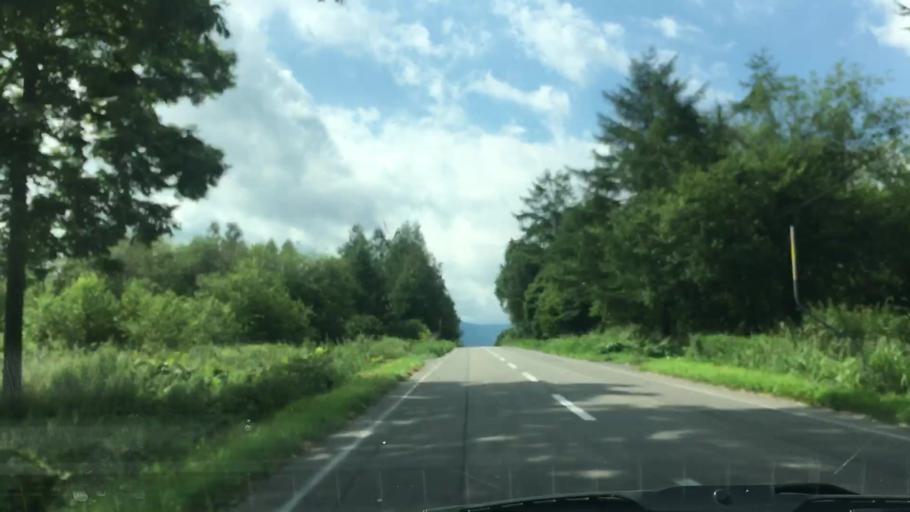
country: JP
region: Hokkaido
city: Otofuke
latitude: 43.2786
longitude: 143.3537
